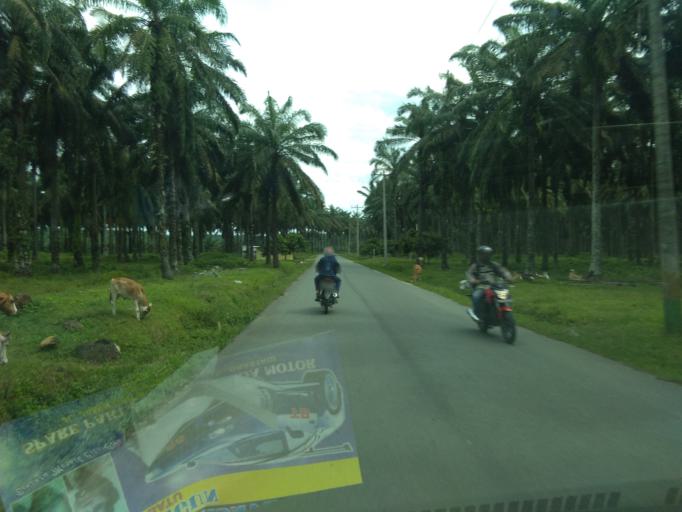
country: ID
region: North Sumatra
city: Deli Tua
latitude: 3.2966
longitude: 98.8076
